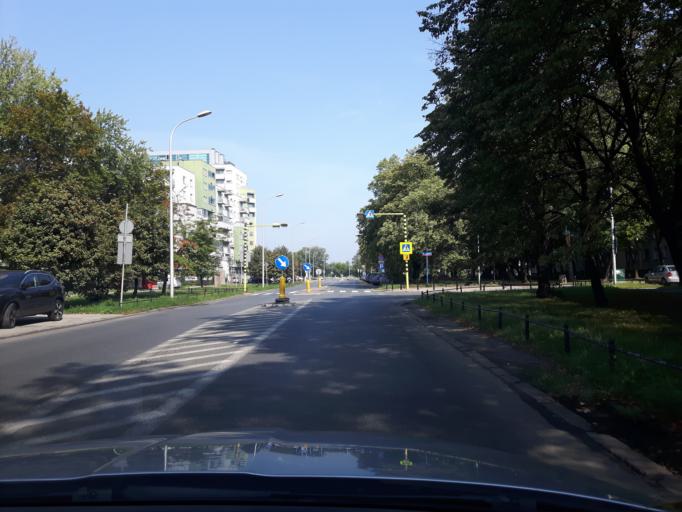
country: PL
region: Masovian Voivodeship
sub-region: Warszawa
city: Targowek
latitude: 52.2979
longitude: 21.0425
